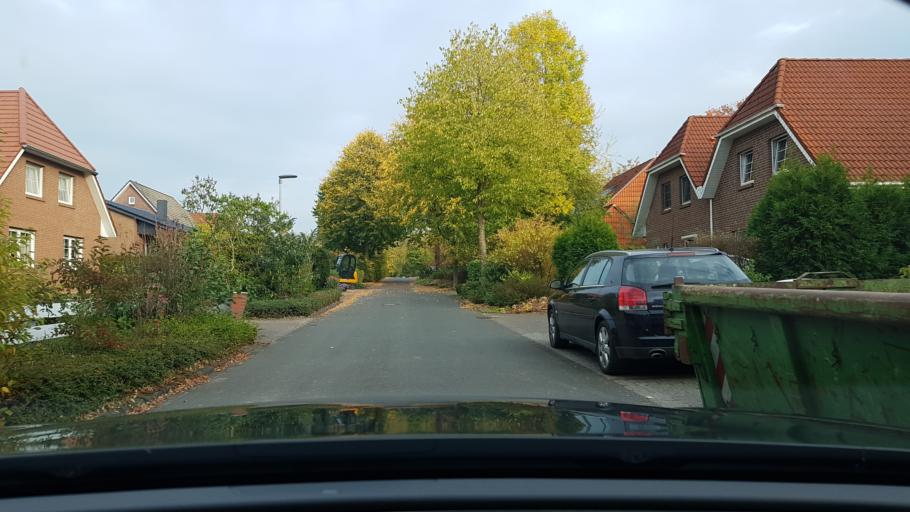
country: DE
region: Lower Saxony
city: Beverstedt
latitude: 53.4284
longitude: 8.8135
